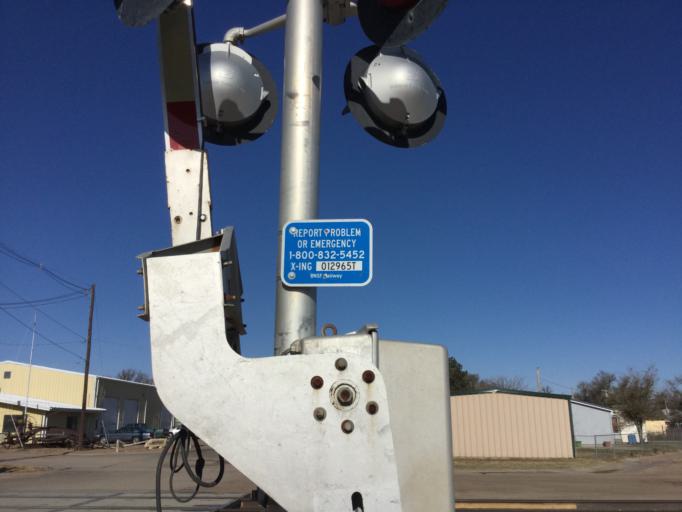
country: US
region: Kansas
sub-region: Kearny County
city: Lakin
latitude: 37.9363
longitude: -101.2590
